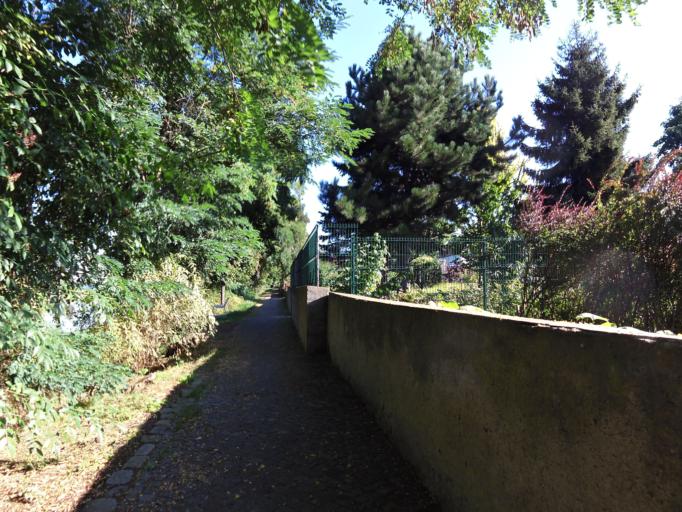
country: DE
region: Saxony
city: Nunchritz
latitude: 51.2664
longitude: 13.4050
